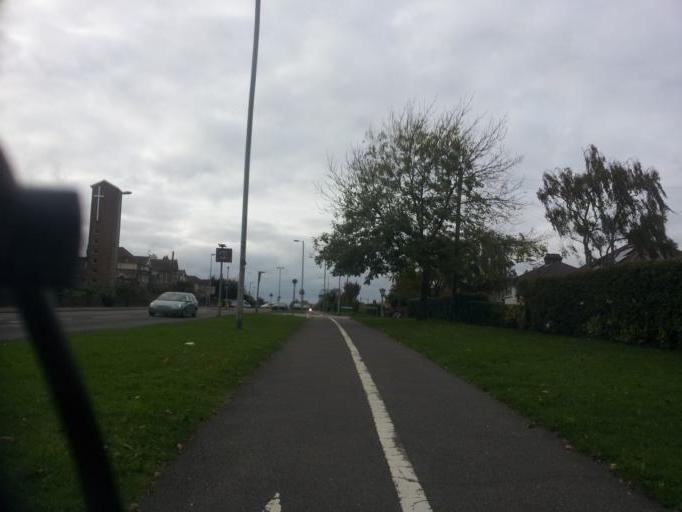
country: GB
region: England
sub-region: Kent
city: Rainham
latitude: 51.3657
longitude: 0.5996
